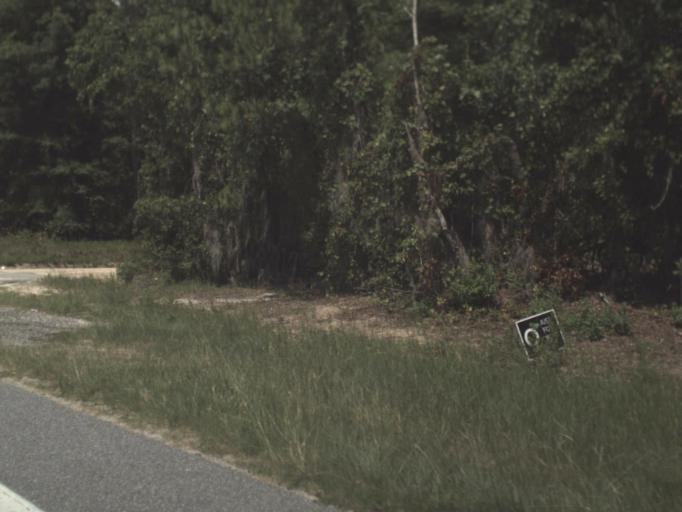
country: US
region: Florida
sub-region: Hamilton County
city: Jasper
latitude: 30.5086
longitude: -83.0661
